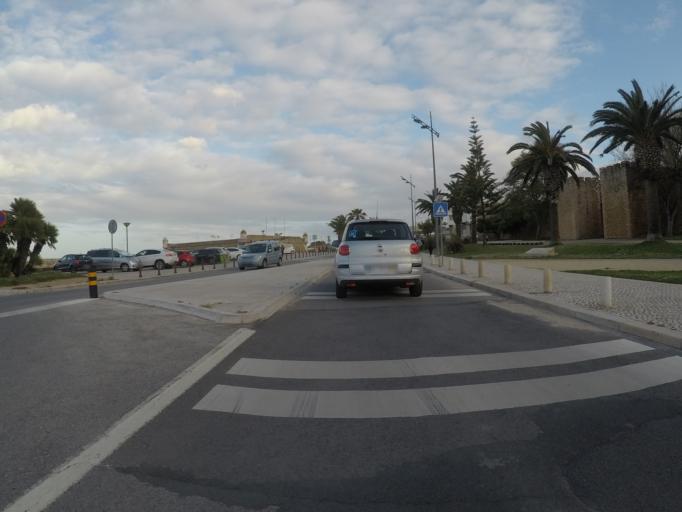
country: PT
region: Faro
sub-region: Lagos
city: Lagos
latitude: 37.0998
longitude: -8.6692
